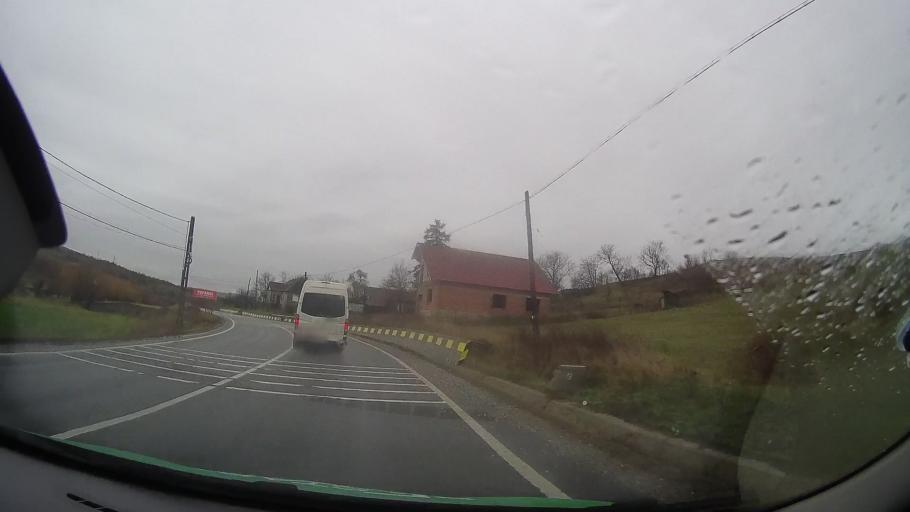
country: RO
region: Bistrita-Nasaud
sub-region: Comuna Galatii Bistritei
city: Galatii Bistritei
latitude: 47.0139
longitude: 24.4079
